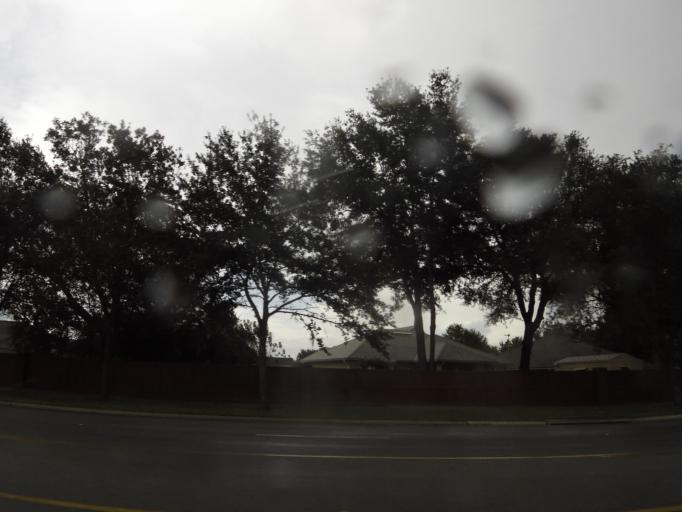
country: US
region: Florida
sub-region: Clay County
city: Asbury Lake
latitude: 30.0336
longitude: -81.8097
